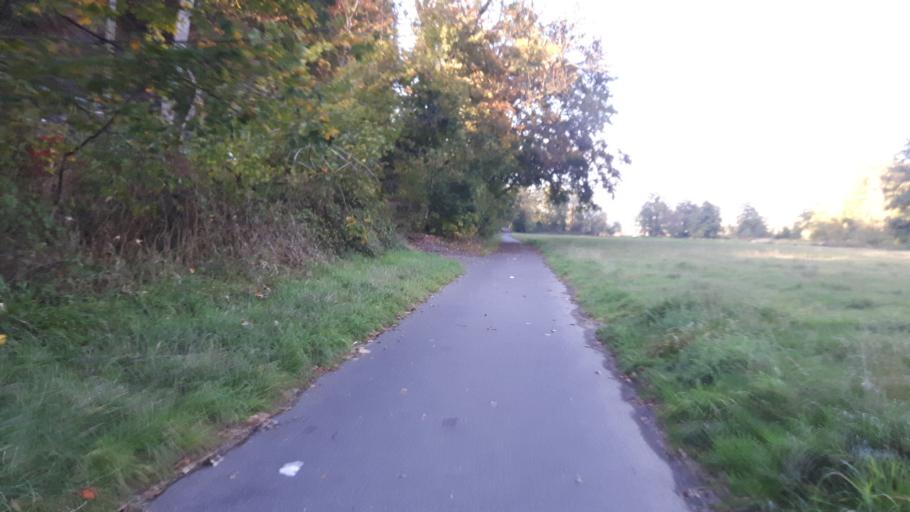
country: DE
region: Rheinland-Pfalz
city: Werkhausen
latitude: 50.7832
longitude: 7.5163
